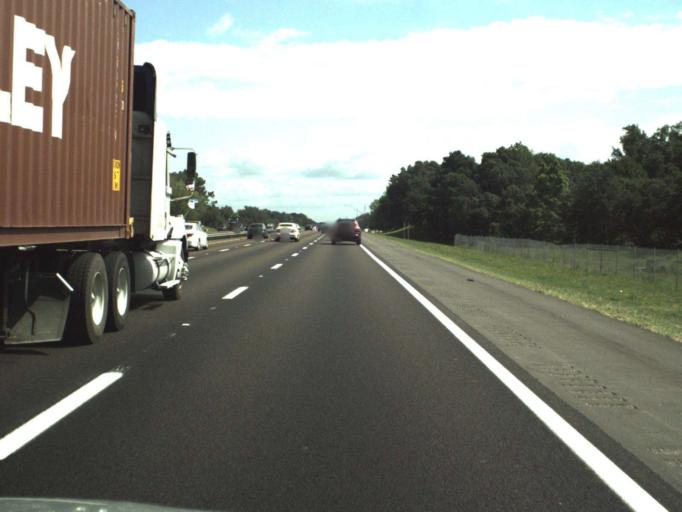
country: US
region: Florida
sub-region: Seminole County
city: Longwood
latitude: 28.7163
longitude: -81.3773
